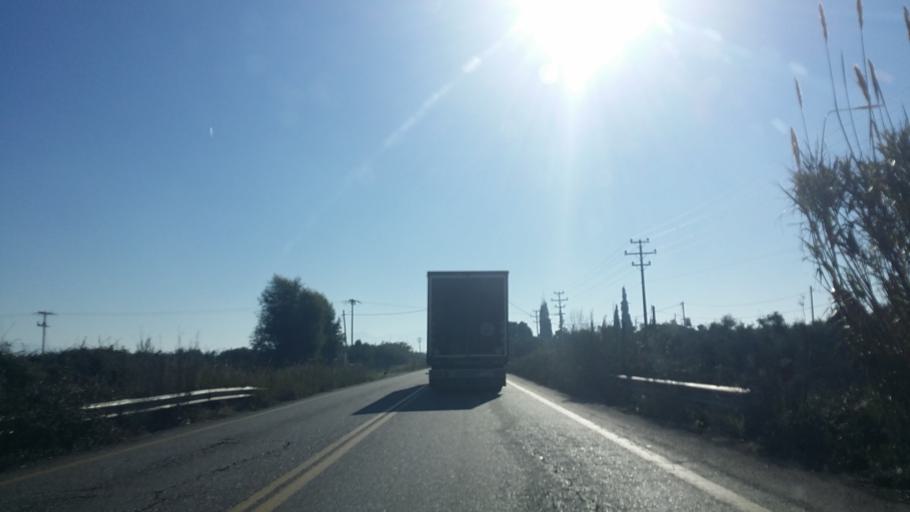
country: GR
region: West Greece
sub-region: Nomos Aitolias kai Akarnanias
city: Mesolongi
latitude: 38.3921
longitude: 21.4297
